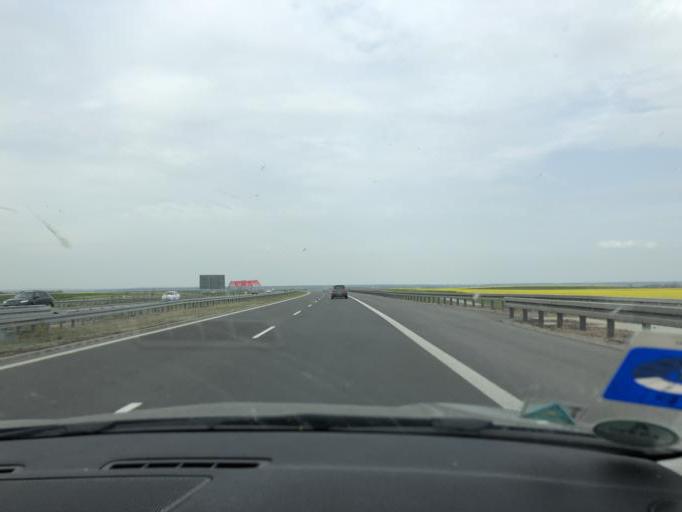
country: PL
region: Subcarpathian Voivodeship
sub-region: Powiat przeworski
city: Mirocin
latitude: 50.0549
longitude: 22.5701
